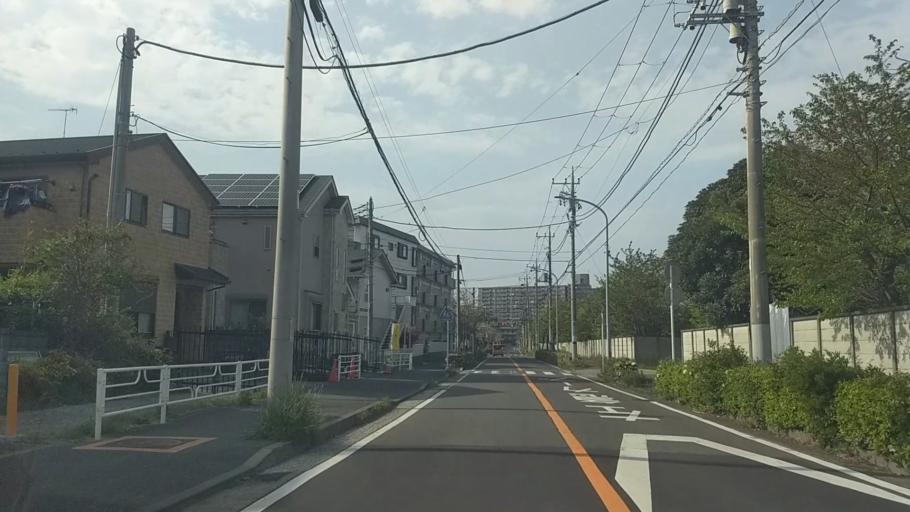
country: JP
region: Kanagawa
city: Kamakura
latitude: 35.3623
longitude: 139.5476
